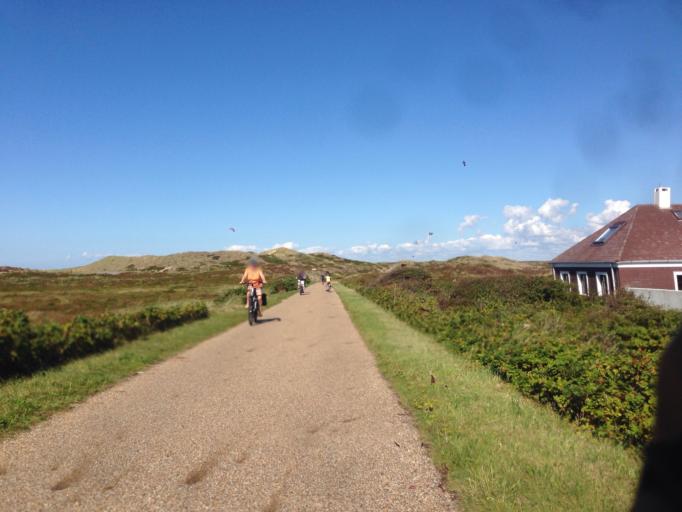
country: DE
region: Schleswig-Holstein
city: Tinnum
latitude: 54.9628
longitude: 8.3405
